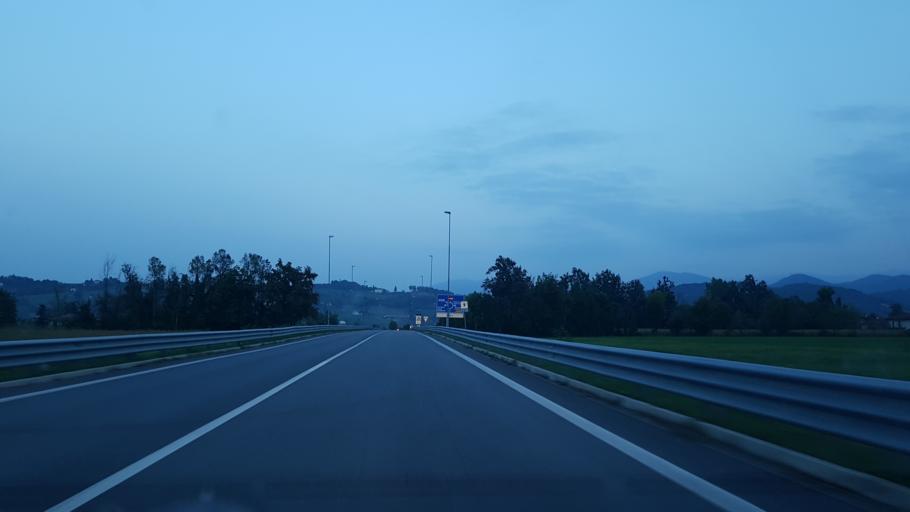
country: IT
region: Piedmont
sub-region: Provincia di Cuneo
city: Villanova Mondovi
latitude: 44.3701
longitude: 7.7943
